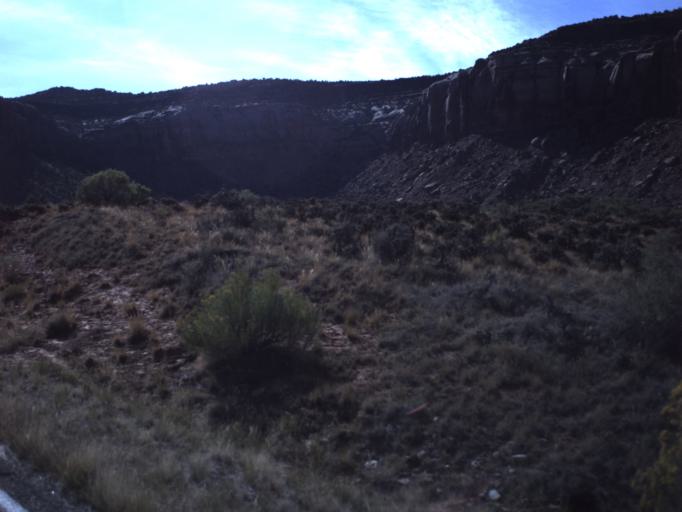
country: US
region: Utah
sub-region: San Juan County
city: Monticello
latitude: 38.0575
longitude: -109.5509
